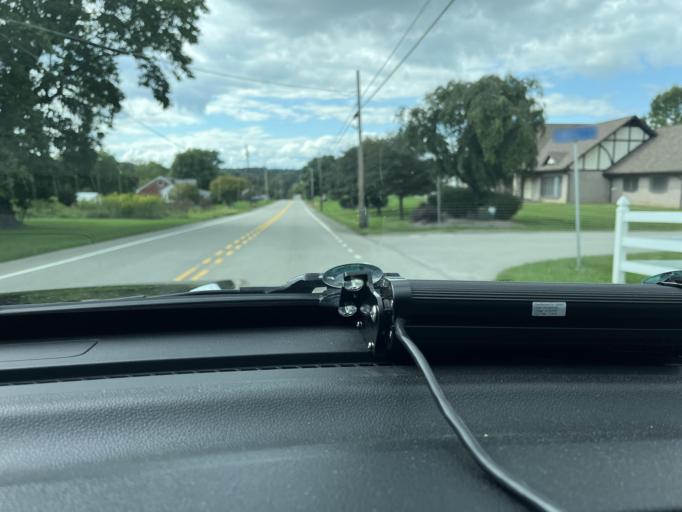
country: US
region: Pennsylvania
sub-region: Fayette County
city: South Uniontown
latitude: 39.9093
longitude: -79.7652
